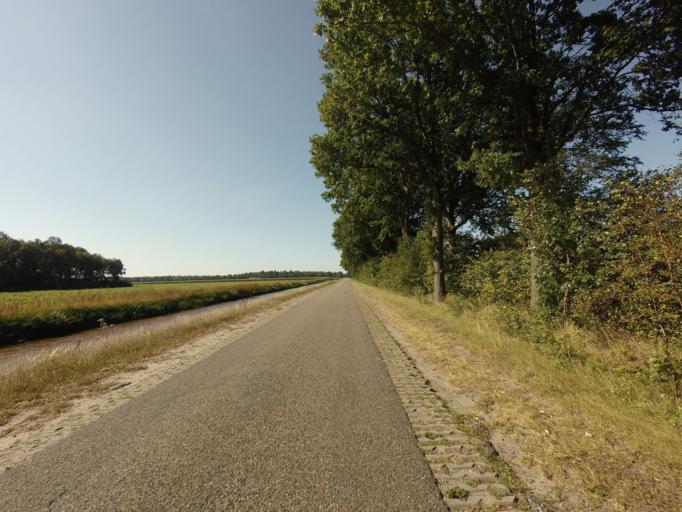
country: NL
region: Overijssel
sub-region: Gemeente Hardenberg
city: Hardenberg
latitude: 52.5269
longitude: 6.6501
